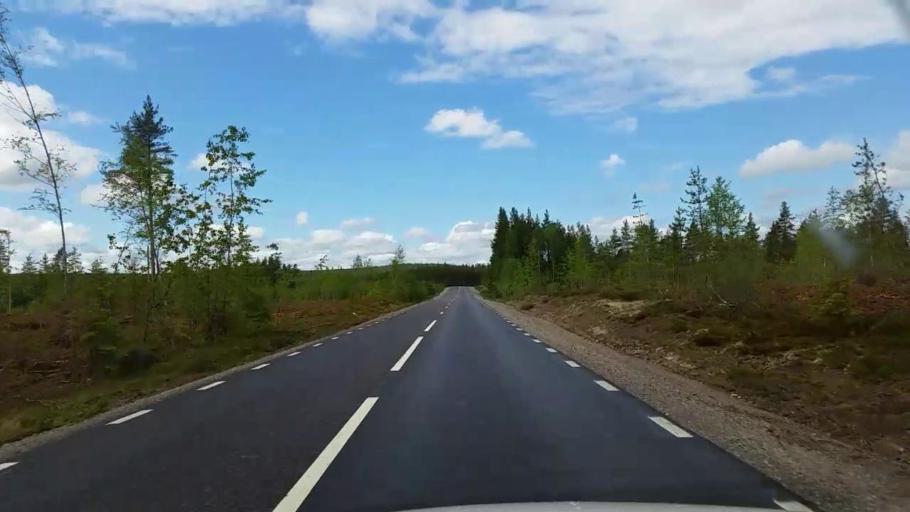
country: SE
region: Gaevleborg
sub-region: Sandvikens Kommun
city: Jarbo
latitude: 60.8780
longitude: 16.3935
